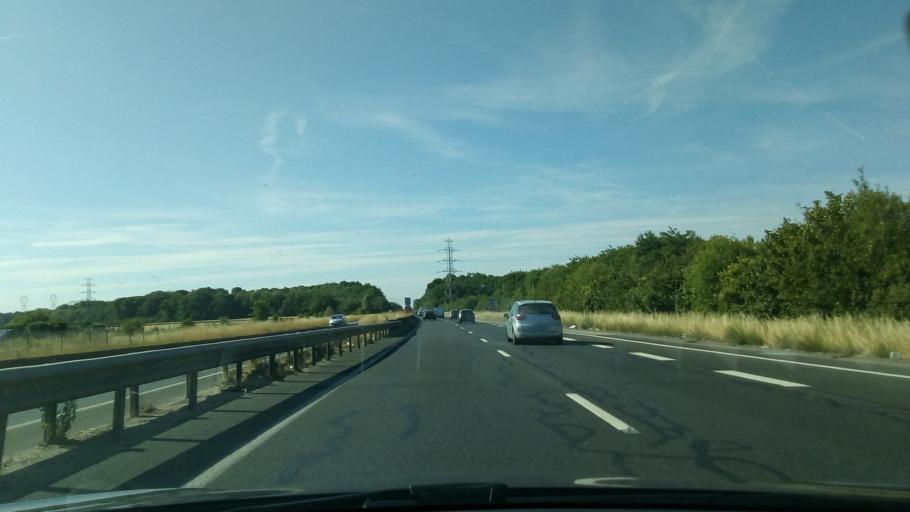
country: FR
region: Ile-de-France
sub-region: Departement de Seine-et-Marne
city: Vert-Saint-Denis
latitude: 48.5700
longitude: 2.6413
